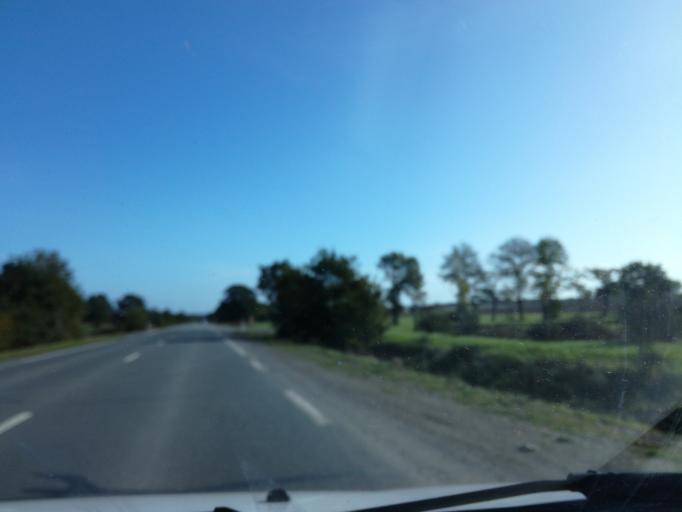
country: FR
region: Brittany
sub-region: Departement d'Ille-et-Vilaine
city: Martigne-Ferchaud
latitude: 47.8211
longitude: -1.3164
